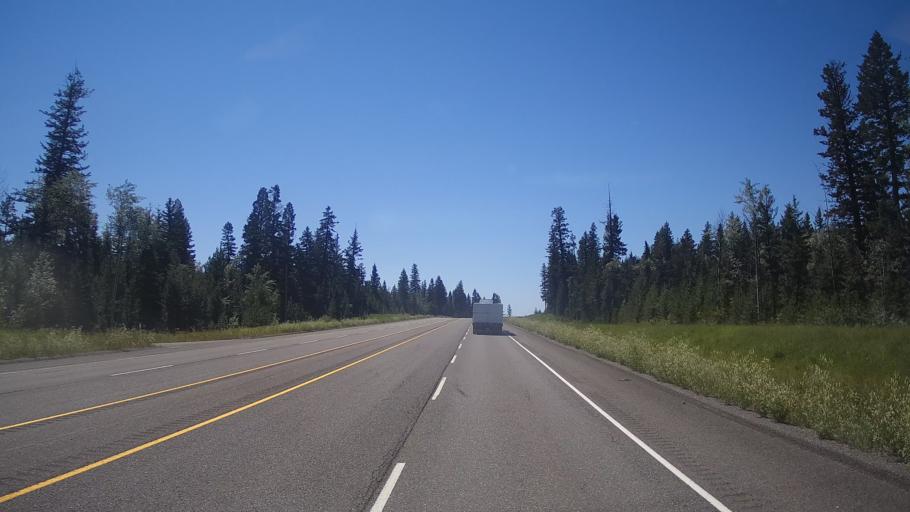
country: CA
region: British Columbia
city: Cache Creek
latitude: 51.4364
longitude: -121.3742
